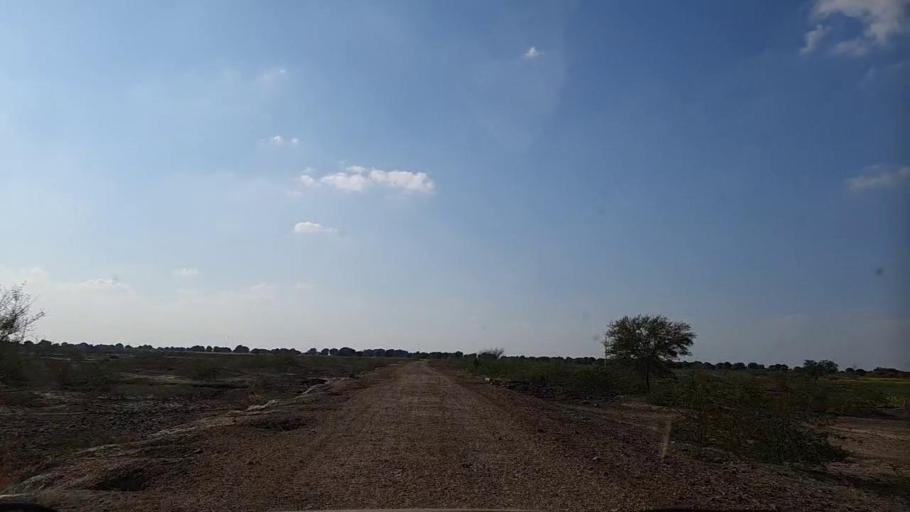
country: PK
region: Sindh
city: Pithoro
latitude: 25.6143
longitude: 69.3617
